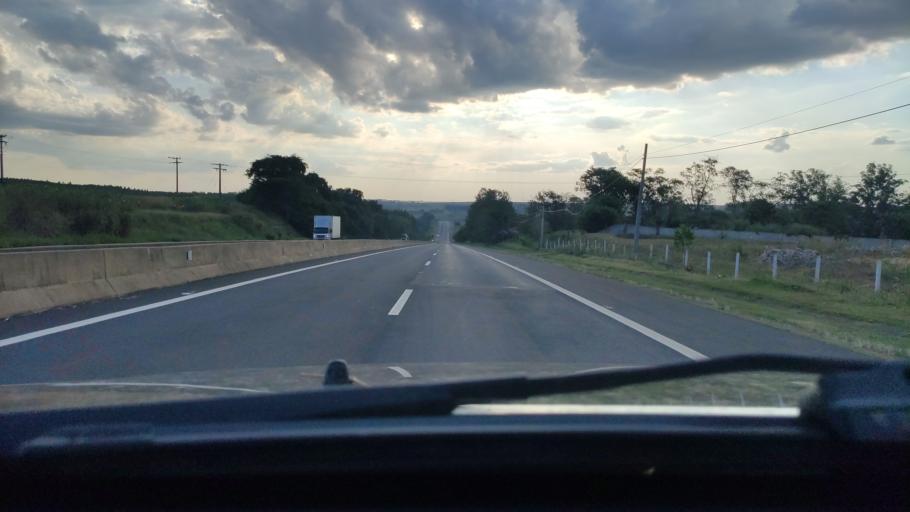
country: BR
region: Sao Paulo
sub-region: Mogi-Mirim
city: Mogi Mirim
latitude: -22.4440
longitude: -47.0319
